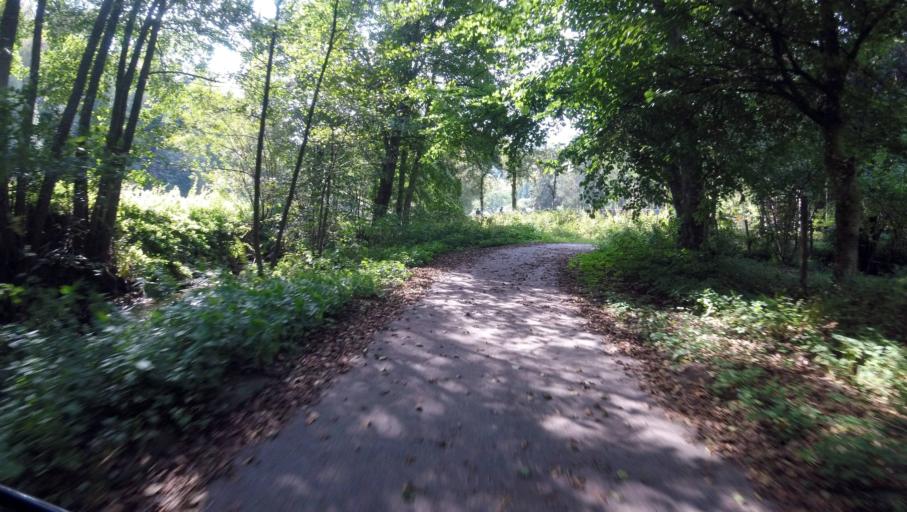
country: DE
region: Baden-Wuerttemberg
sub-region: Karlsruhe Region
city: Wornersberg
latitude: 48.5825
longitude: 8.5754
